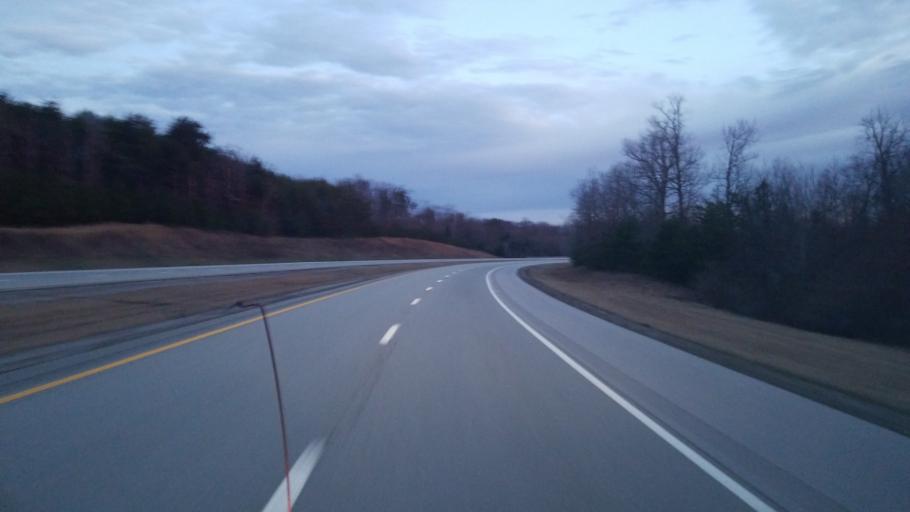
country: US
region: Tennessee
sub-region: Van Buren County
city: Spencer
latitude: 35.6938
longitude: -85.4812
